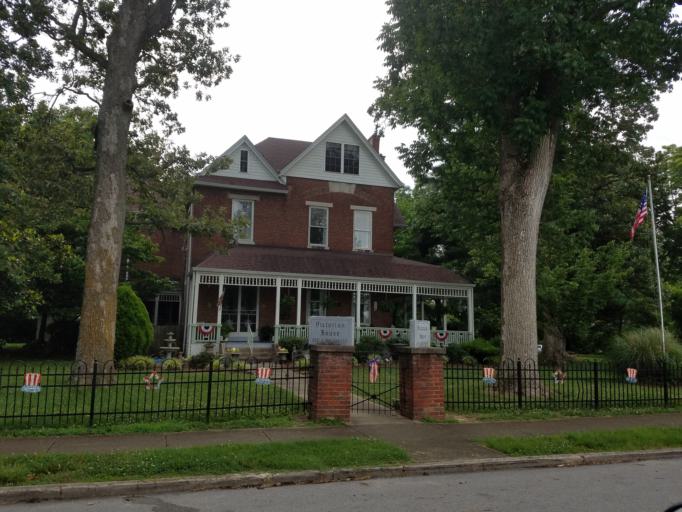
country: US
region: Kentucky
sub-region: Edmonson County
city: Brownsville
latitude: 37.0535
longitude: -86.2084
